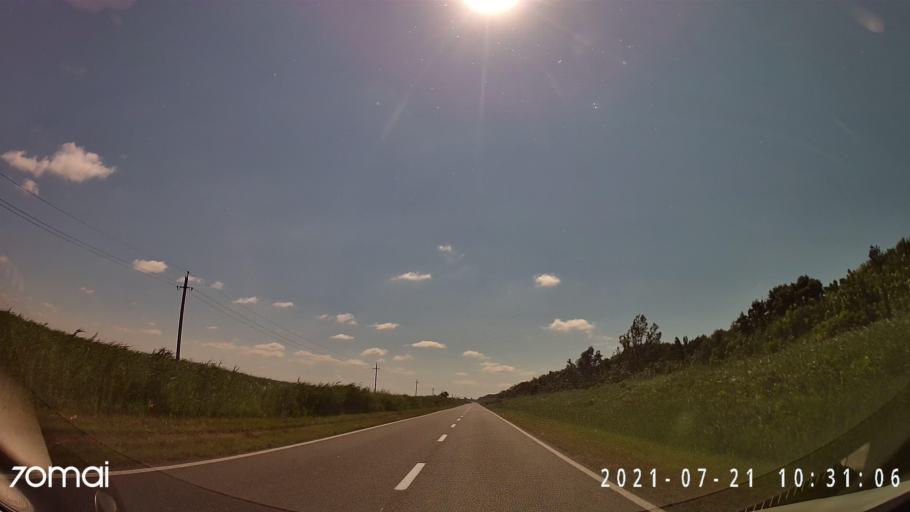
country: RO
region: Tulcea
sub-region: Comuna Luncavita
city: Rachelu
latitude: 45.3107
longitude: 28.3933
